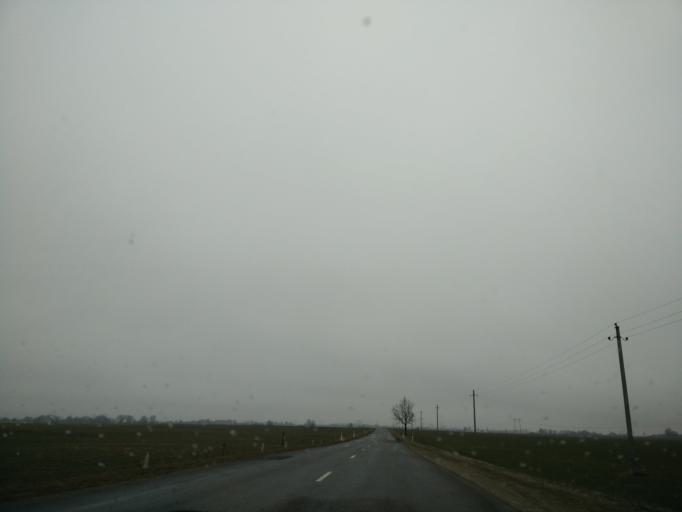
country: LT
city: Ariogala
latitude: 55.3093
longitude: 23.4323
